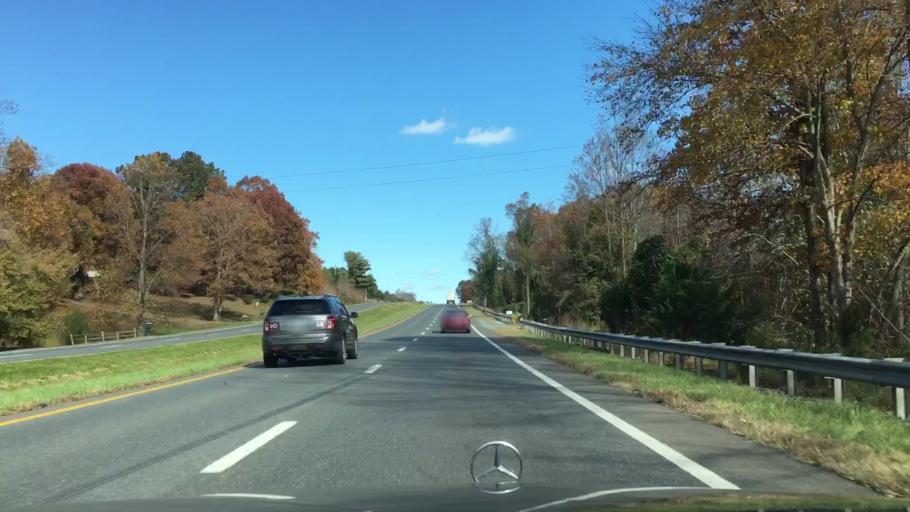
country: US
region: Virginia
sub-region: Campbell County
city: Rustburg
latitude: 37.2623
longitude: -79.1803
